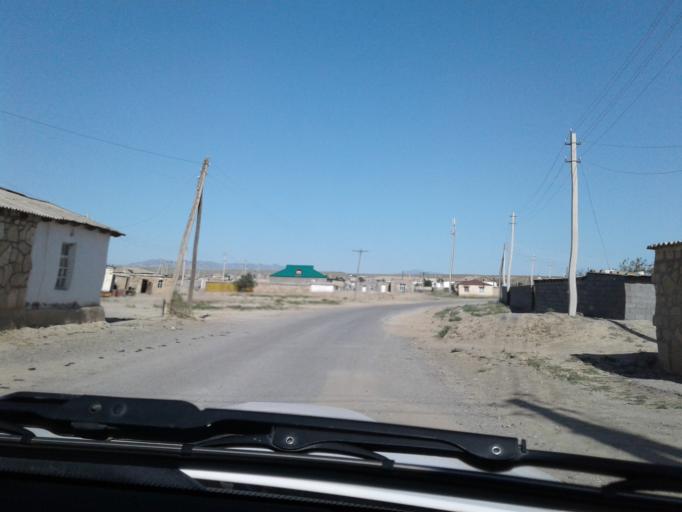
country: TM
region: Balkan
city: Serdar
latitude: 38.7138
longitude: 56.3354
